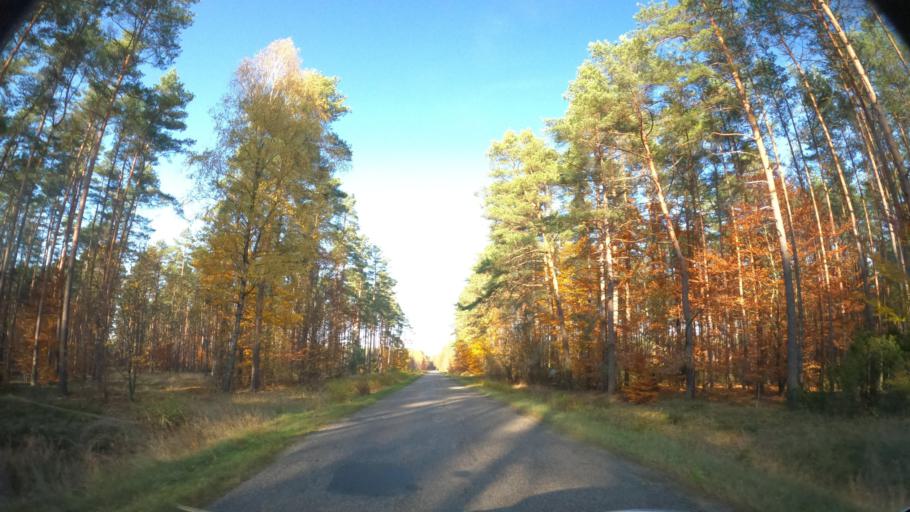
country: PL
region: Greater Poland Voivodeship
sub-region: Powiat zlotowski
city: Sypniewo
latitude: 53.3892
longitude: 16.5743
